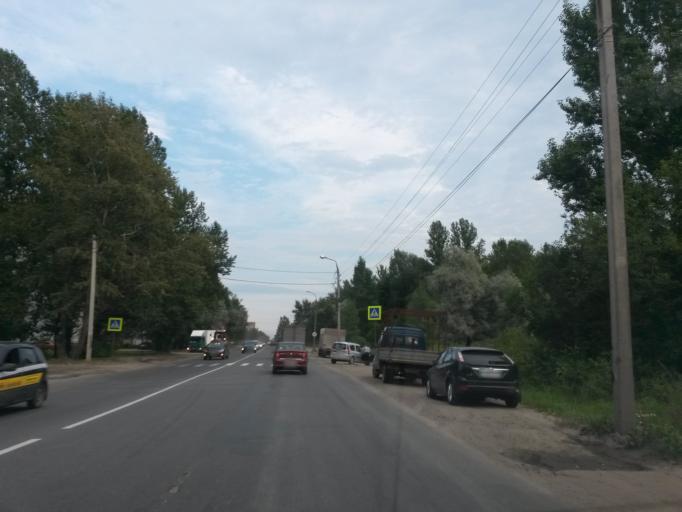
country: RU
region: Jaroslavl
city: Yaroslavl
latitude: 57.5831
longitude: 39.8254
